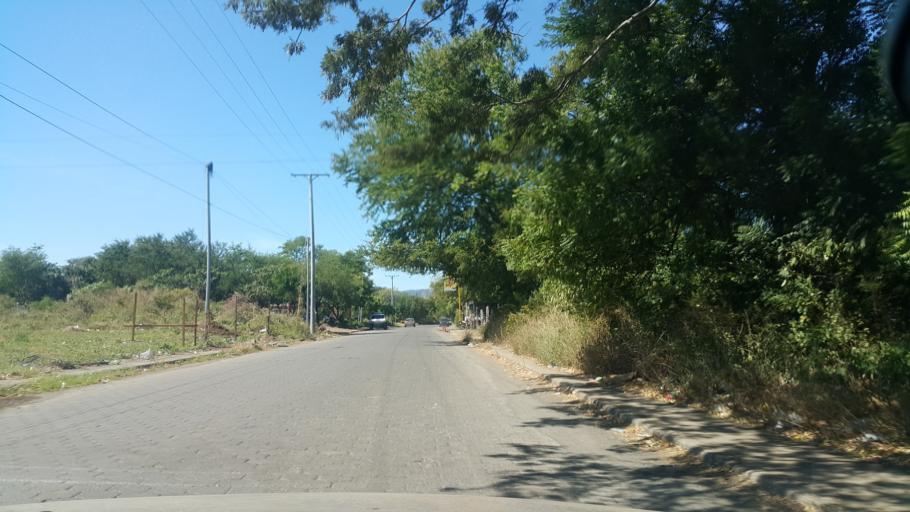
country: NI
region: Managua
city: Ciudad Sandino
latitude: 12.1467
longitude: -86.3396
